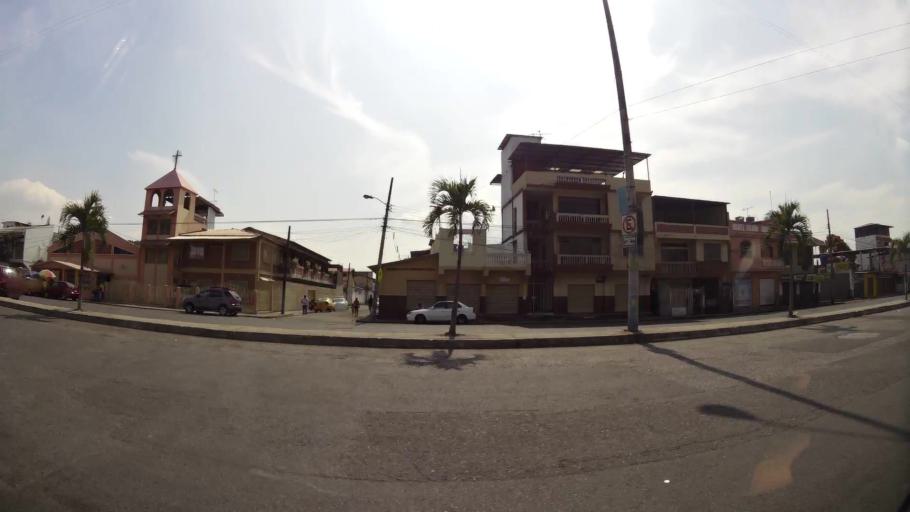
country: EC
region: Guayas
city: Guayaquil
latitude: -2.2632
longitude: -79.8897
